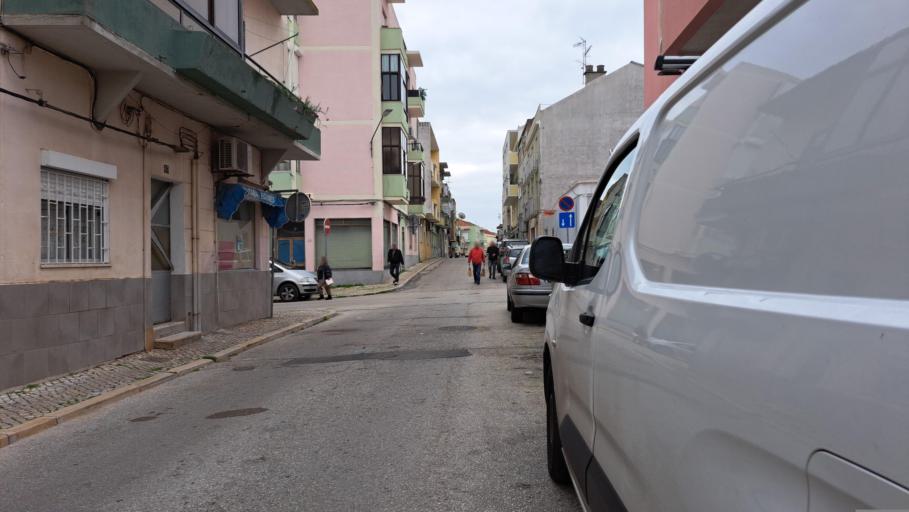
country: PT
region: Setubal
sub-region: Moita
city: Alhos Vedros
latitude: 38.6577
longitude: -9.0446
